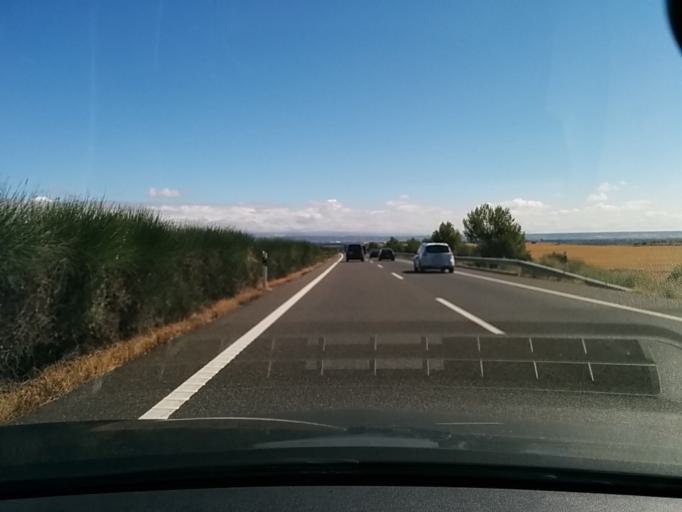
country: ES
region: Aragon
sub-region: Provincia de Huesca
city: Sangarren
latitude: 42.0777
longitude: -0.4946
